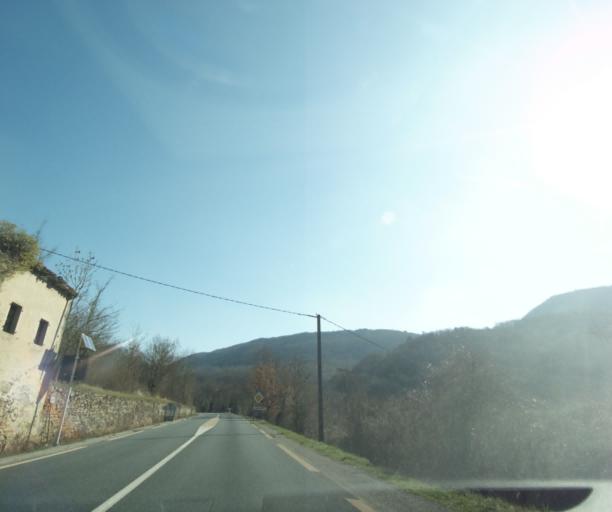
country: FR
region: Midi-Pyrenees
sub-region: Departement de l'Aveyron
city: Saint-Affrique
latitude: 43.9463
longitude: 2.9043
